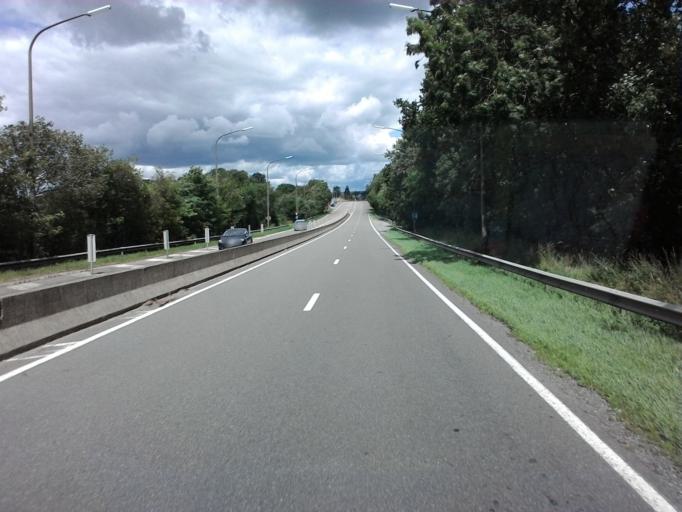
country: BE
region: Wallonia
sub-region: Province du Luxembourg
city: Fauvillers
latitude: 49.8936
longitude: 5.7011
